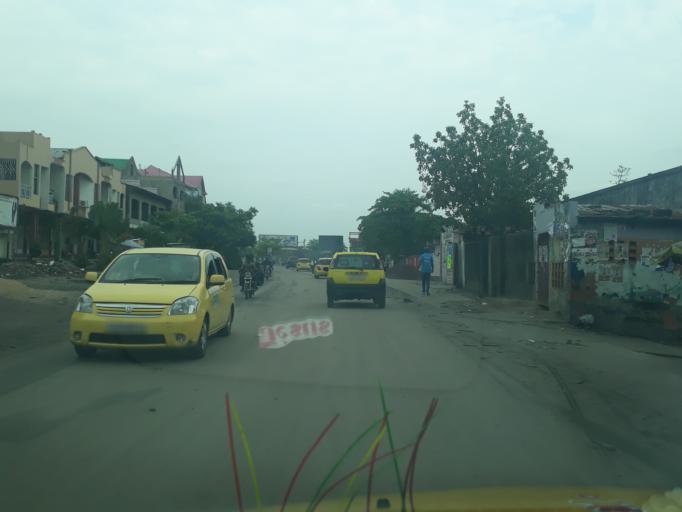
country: CD
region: Kinshasa
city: Kinshasa
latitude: -4.3408
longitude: 15.3042
